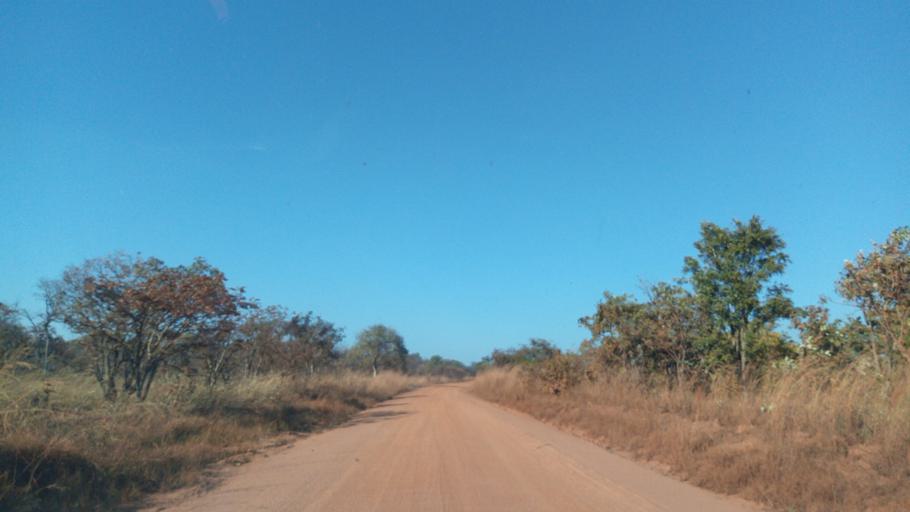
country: ZM
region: Luapula
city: Mwense
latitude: -10.5544
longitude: 28.4434
